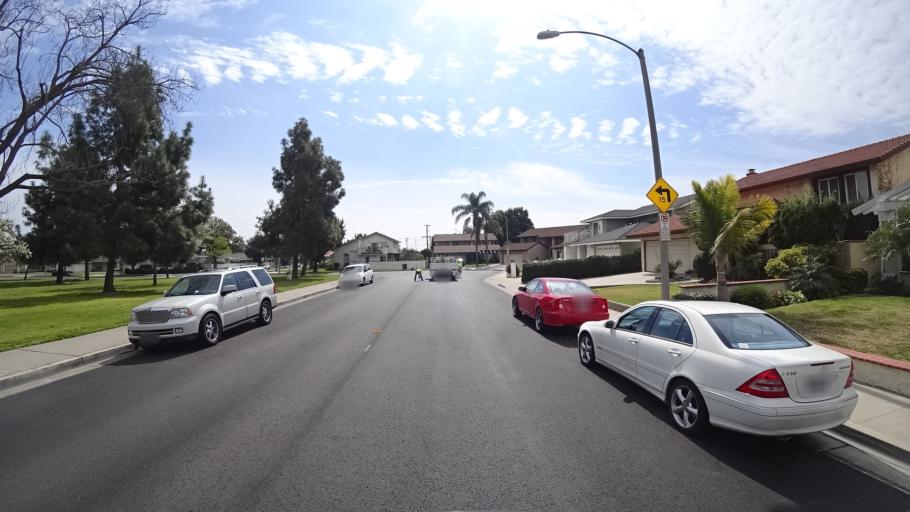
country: US
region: California
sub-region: Orange County
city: Stanton
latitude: 33.8139
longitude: -117.9545
